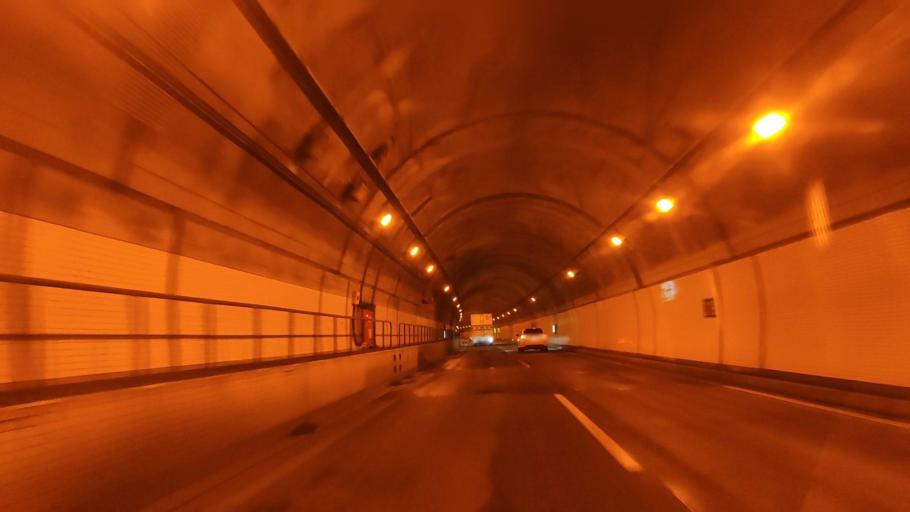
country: JP
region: Niigata
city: Itoigawa
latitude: 37.0539
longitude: 137.9247
